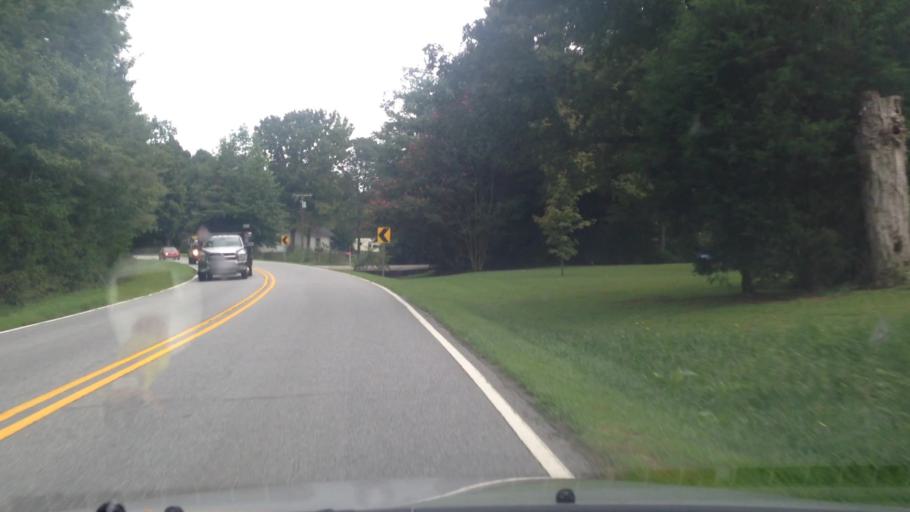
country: US
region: North Carolina
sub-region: Forsyth County
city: Walkertown
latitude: 36.2109
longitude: -80.1689
